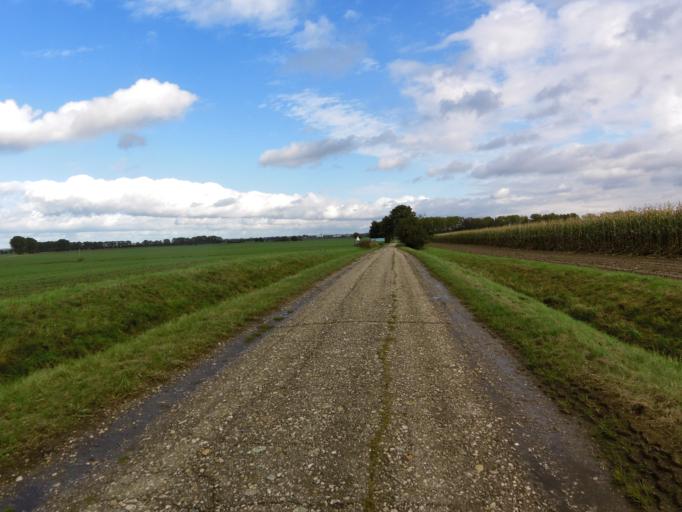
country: DE
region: Saxony
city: Grossposna
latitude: 51.3118
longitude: 12.4854
